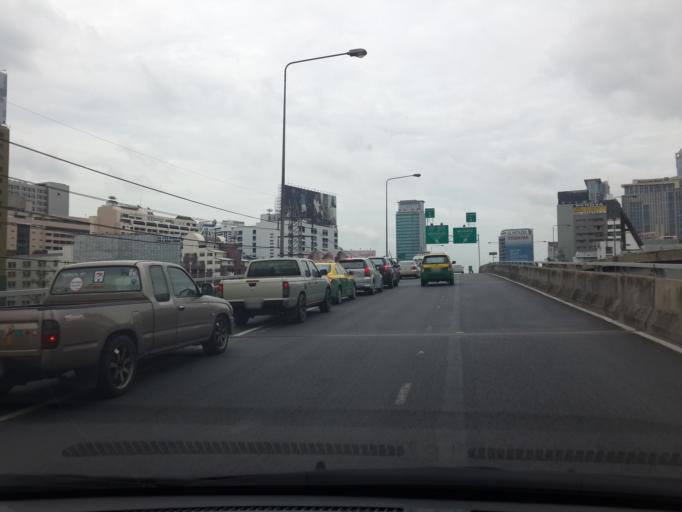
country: TH
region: Bangkok
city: Ratchathewi
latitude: 13.7483
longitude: 100.5500
